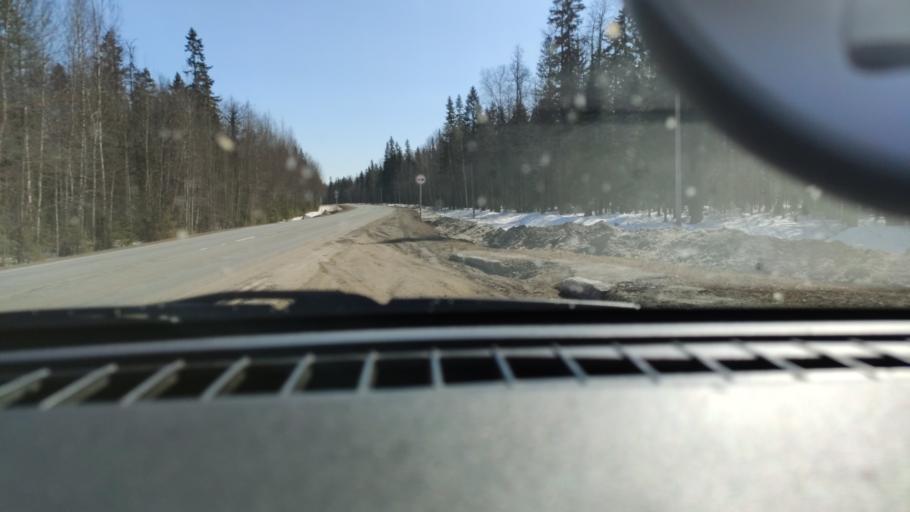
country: RU
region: Perm
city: Perm
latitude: 58.2201
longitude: 56.1678
